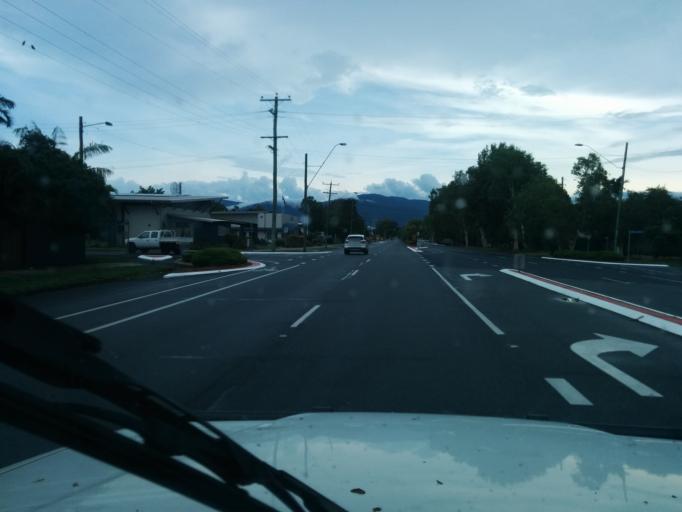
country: AU
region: Queensland
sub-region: Cairns
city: Cairns
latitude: -16.9236
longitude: 145.7493
